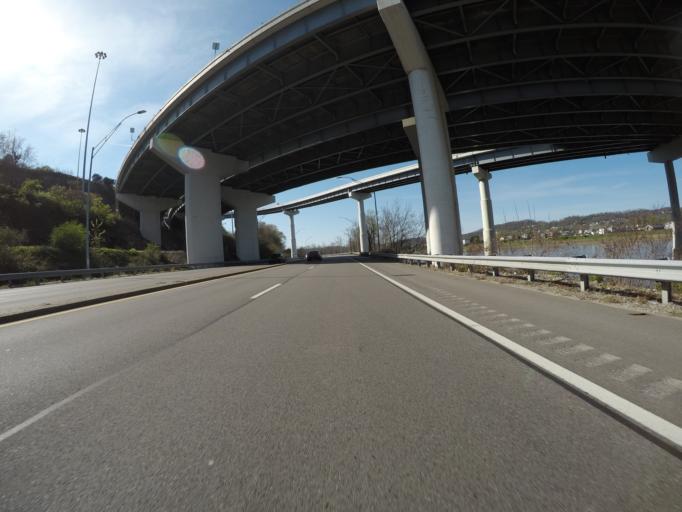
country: US
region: West Virginia
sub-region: Kanawha County
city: Charleston
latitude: 38.3543
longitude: -81.6499
